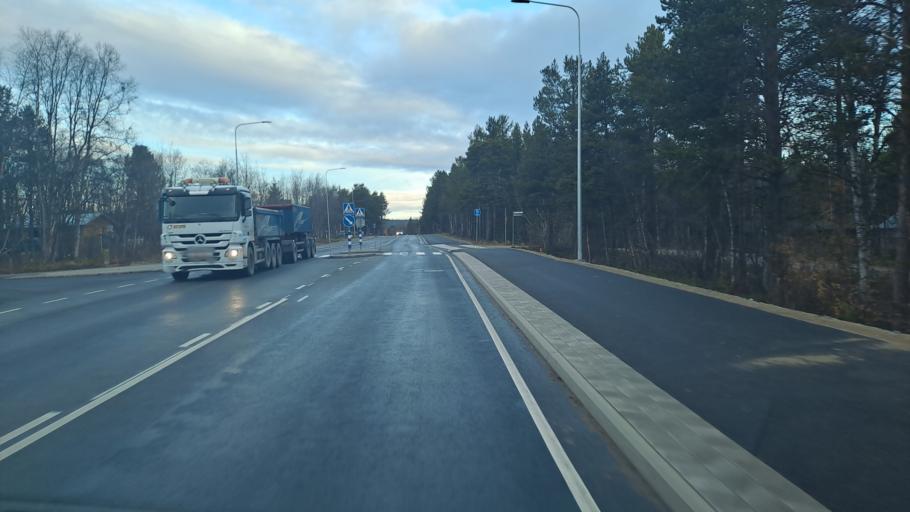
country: FI
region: Lapland
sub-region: Pohjois-Lappi
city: Inari
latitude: 68.9031
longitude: 27.0338
